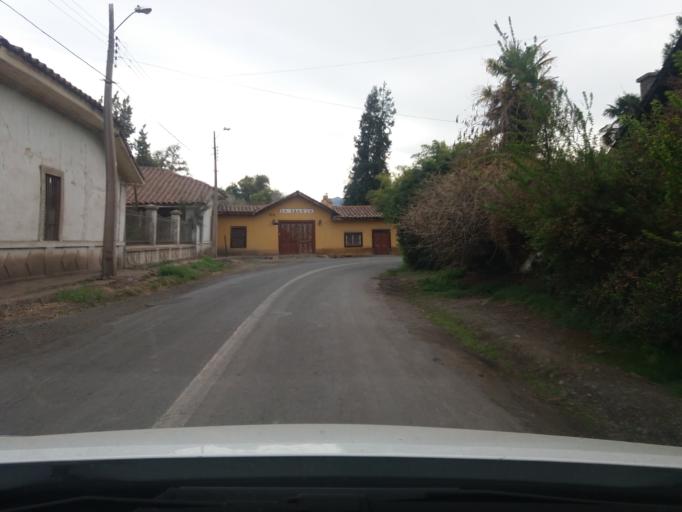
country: CL
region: Valparaiso
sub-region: Provincia de Los Andes
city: Los Andes
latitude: -32.8572
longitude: -70.6499
